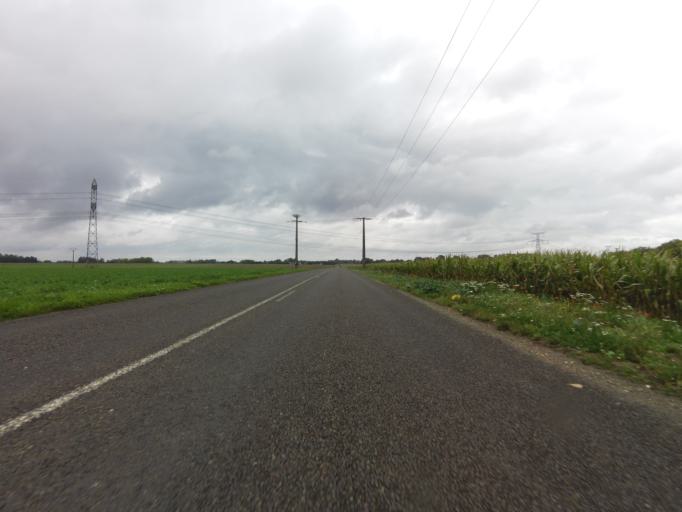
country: FR
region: Haute-Normandie
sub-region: Departement de la Seine-Maritime
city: Totes
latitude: 49.7048
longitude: 1.0478
